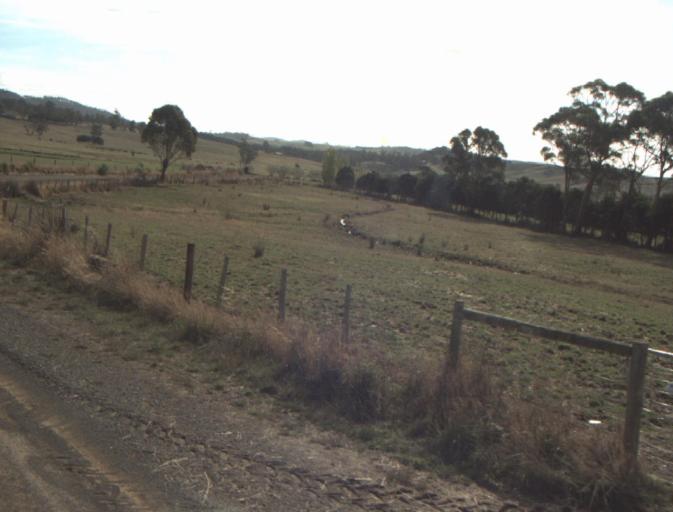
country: AU
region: Tasmania
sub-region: Launceston
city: Mayfield
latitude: -41.2188
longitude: 147.1624
